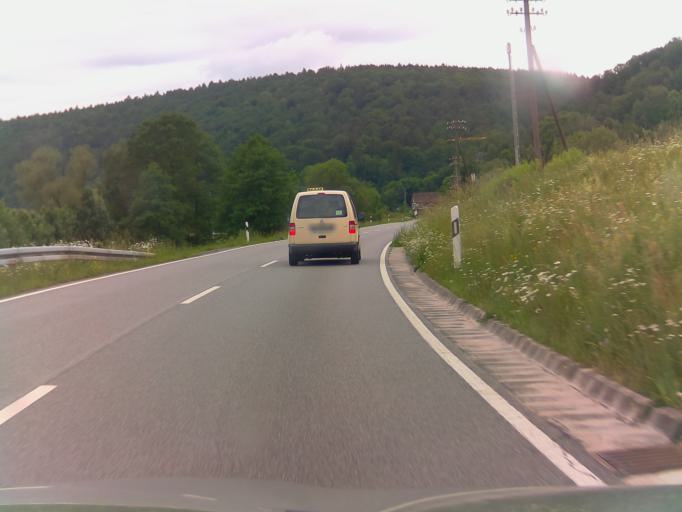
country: DE
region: Bavaria
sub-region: Regierungsbezirk Unterfranken
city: Grafendorf
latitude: 50.1130
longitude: 9.7302
